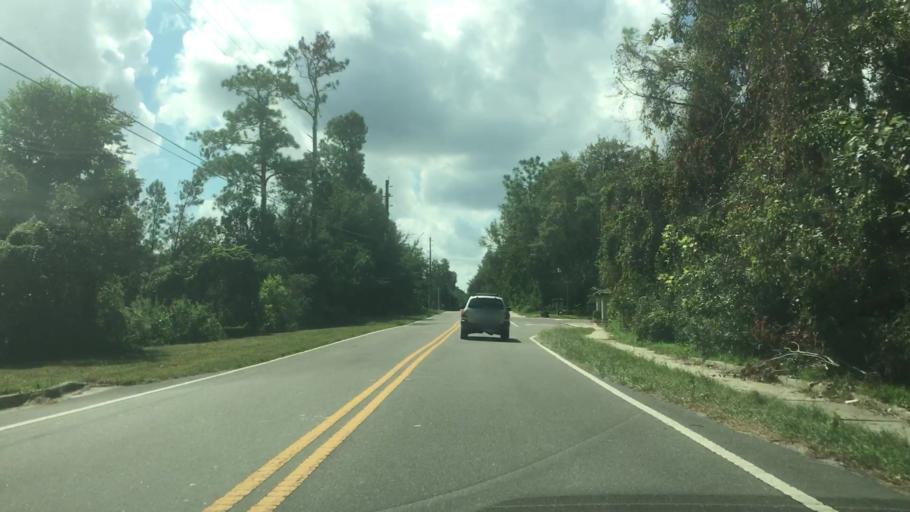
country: US
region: Florida
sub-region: Duval County
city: Jacksonville
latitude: 30.4507
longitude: -81.5791
